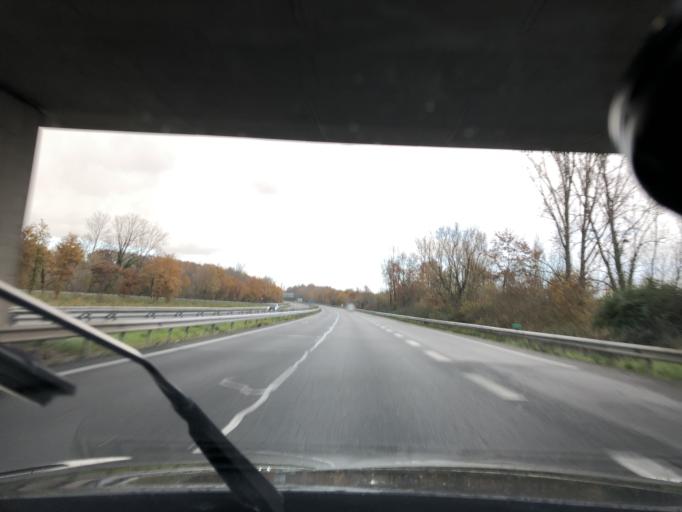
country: FR
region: Aquitaine
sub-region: Departement du Lot-et-Garonne
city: Fourques-sur-Garonne
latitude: 44.4302
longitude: 0.1348
